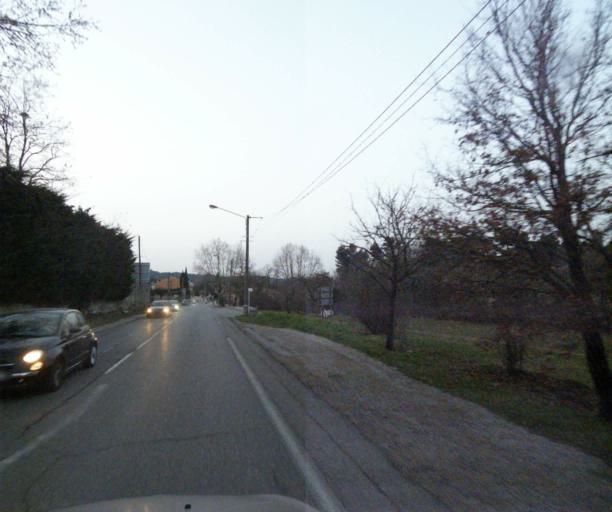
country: FR
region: Provence-Alpes-Cote d'Azur
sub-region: Departement des Bouches-du-Rhone
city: Gardanne
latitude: 43.4301
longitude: 5.4696
